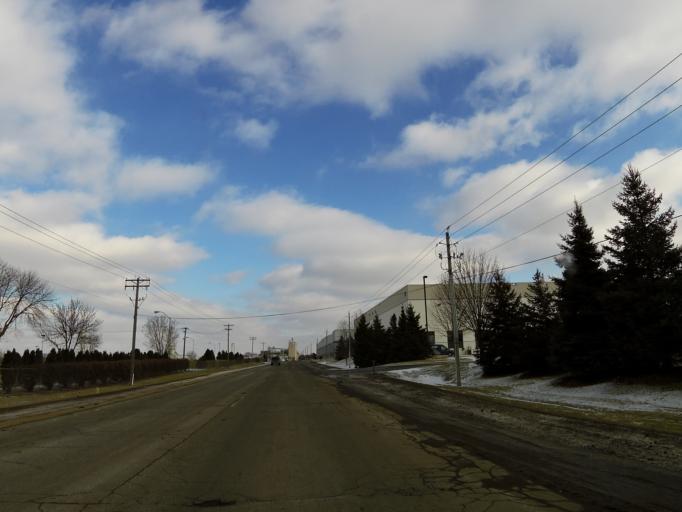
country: US
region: Minnesota
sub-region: Scott County
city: Shakopee
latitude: 44.7975
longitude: -93.4797
